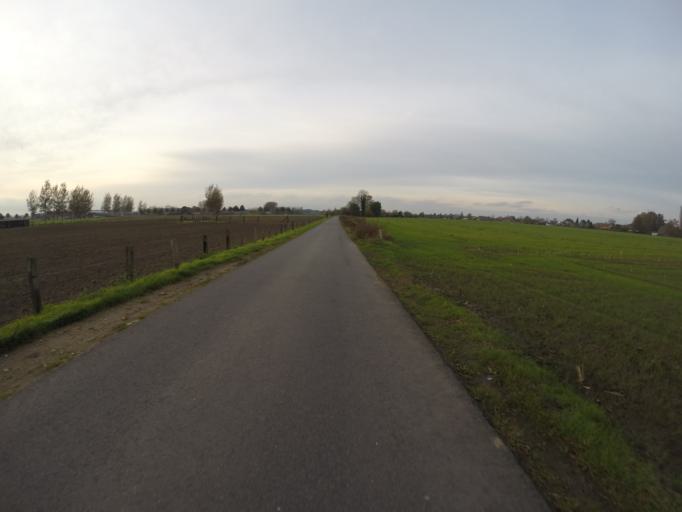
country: BE
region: Flanders
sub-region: Provincie Oost-Vlaanderen
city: Aalter
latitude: 51.0656
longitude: 3.4430
